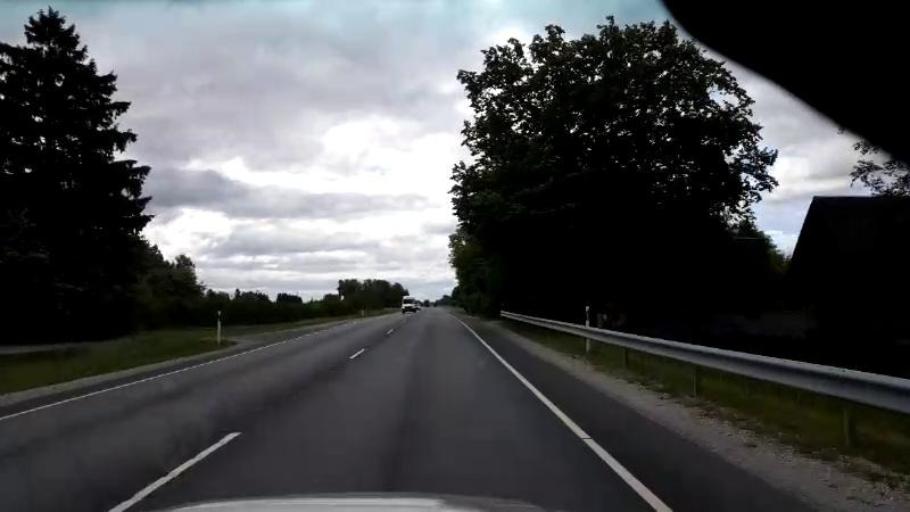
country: EE
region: Paernumaa
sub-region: Halinga vald
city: Parnu-Jaagupi
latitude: 58.6503
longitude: 24.4805
